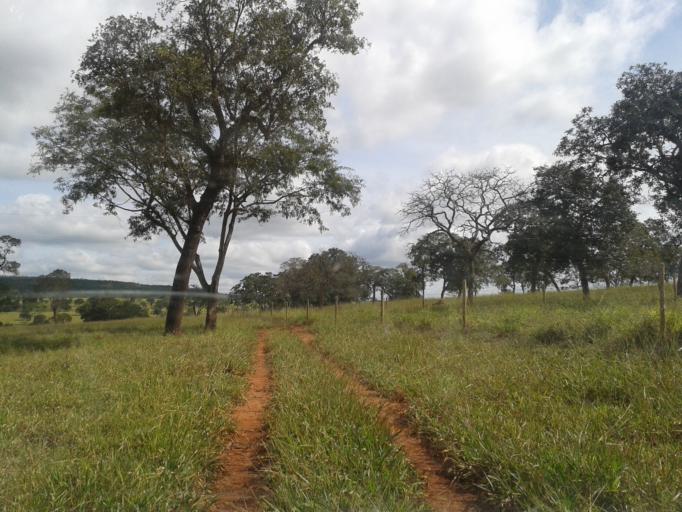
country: BR
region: Minas Gerais
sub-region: Campina Verde
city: Campina Verde
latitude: -19.4279
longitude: -49.7021
